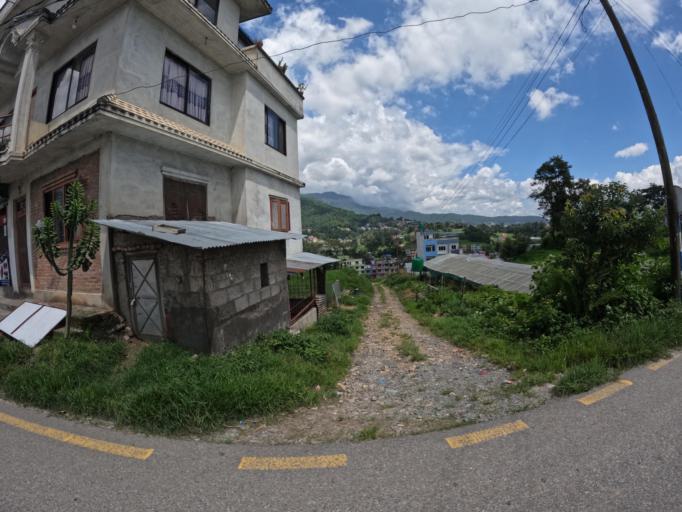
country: NP
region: Central Region
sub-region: Bagmati Zone
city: Kathmandu
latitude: 27.7765
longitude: 85.3272
